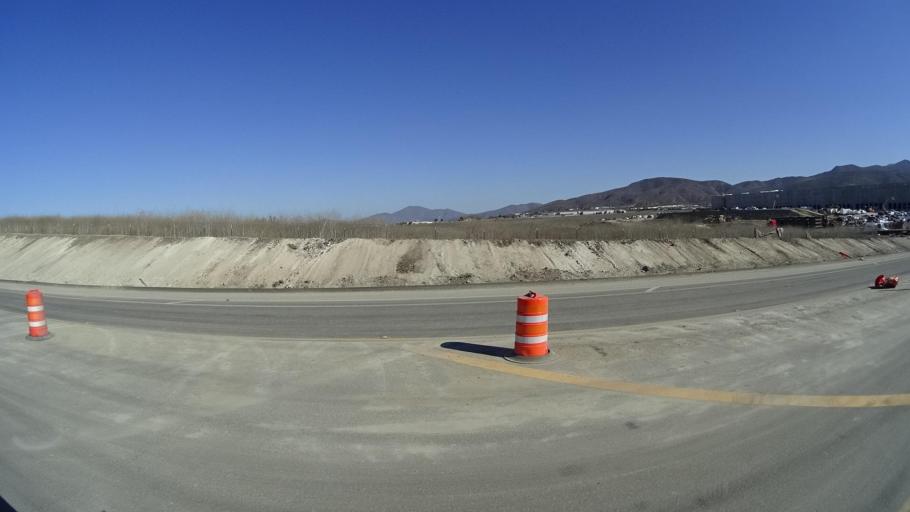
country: MX
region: Baja California
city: Tijuana
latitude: 32.5674
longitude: -116.9288
